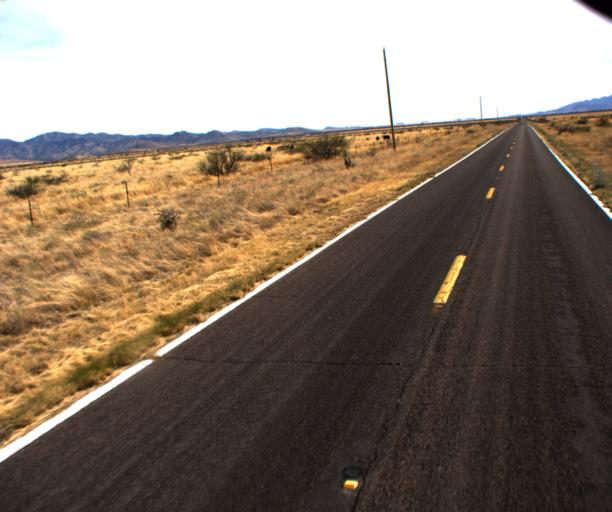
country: US
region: Arizona
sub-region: Cochise County
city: Willcox
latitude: 31.9284
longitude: -109.4914
